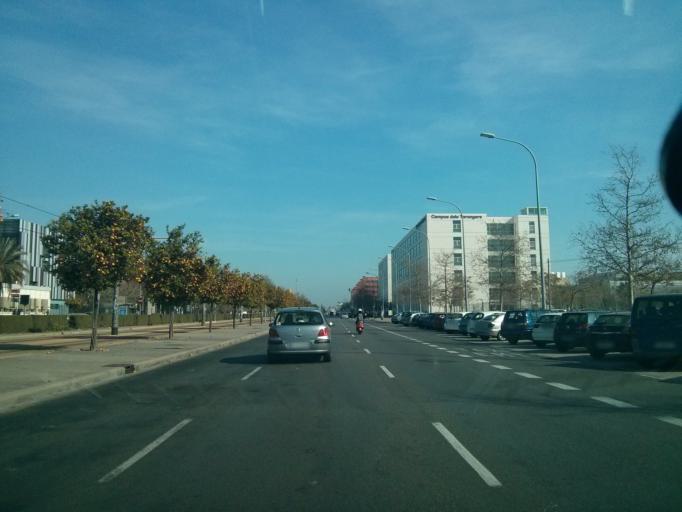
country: ES
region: Valencia
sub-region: Provincia de Valencia
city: Alboraya
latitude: 39.4808
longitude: -0.3491
